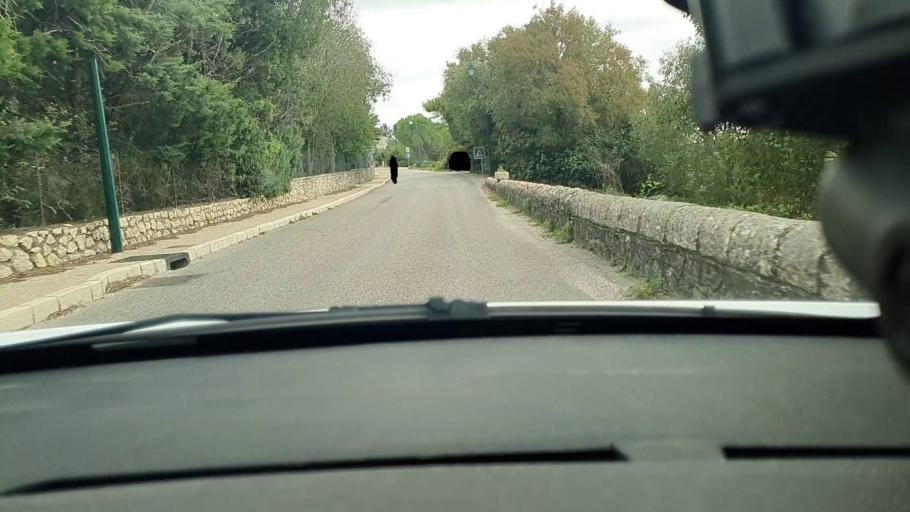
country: FR
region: Languedoc-Roussillon
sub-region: Departement du Gard
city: Salindres
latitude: 44.1654
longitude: 4.2389
